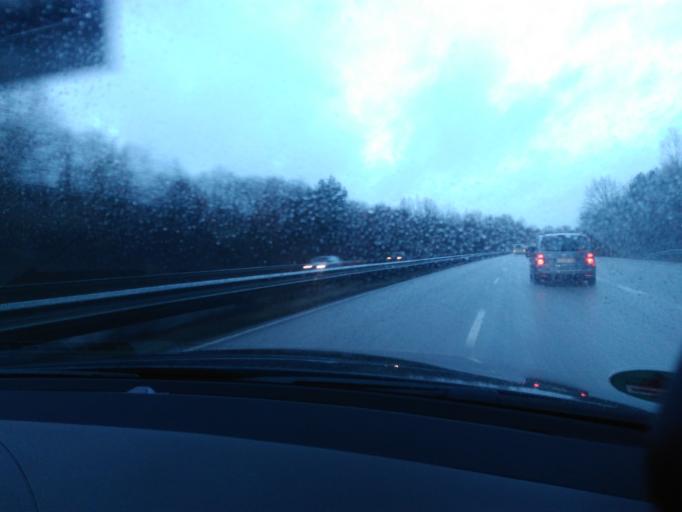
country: DE
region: Schleswig-Holstein
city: Kronshagen
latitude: 54.3204
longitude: 10.0984
